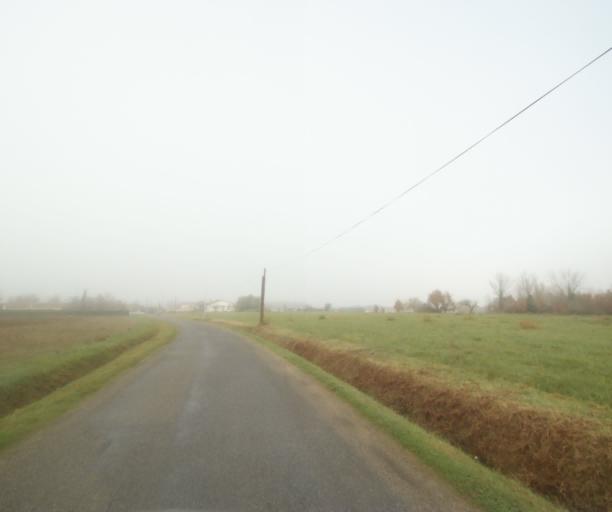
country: FR
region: Midi-Pyrenees
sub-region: Departement de la Haute-Garonne
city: Villaudric
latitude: 43.8337
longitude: 1.4654
